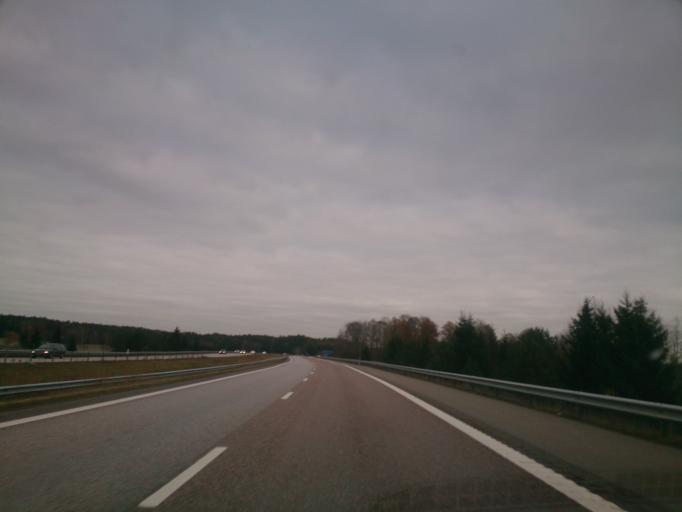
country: SE
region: Soedermanland
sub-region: Gnesta Kommun
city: Gnesta
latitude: 58.9009
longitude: 17.3059
